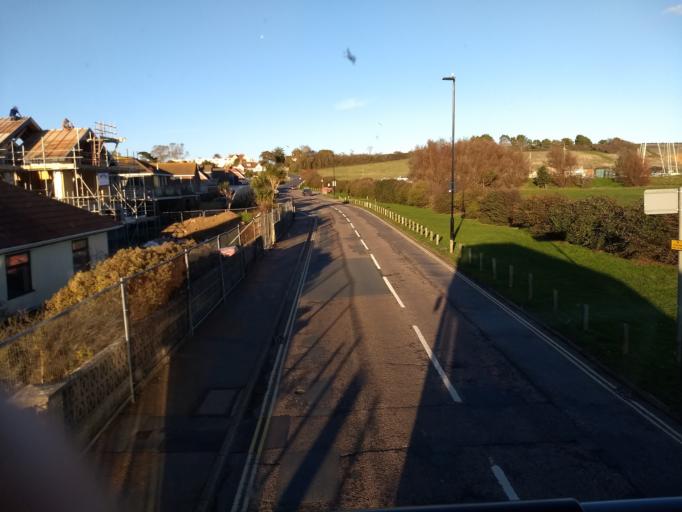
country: GB
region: England
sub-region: Isle of Wight
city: Brading
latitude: 50.6618
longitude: -1.1362
